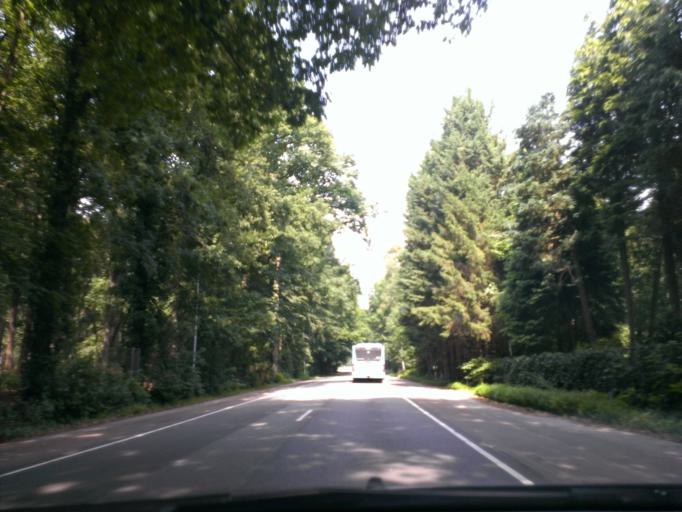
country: NL
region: Gelderland
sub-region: Gemeente Hattem
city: Hattem
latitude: 52.4351
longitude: 6.0692
